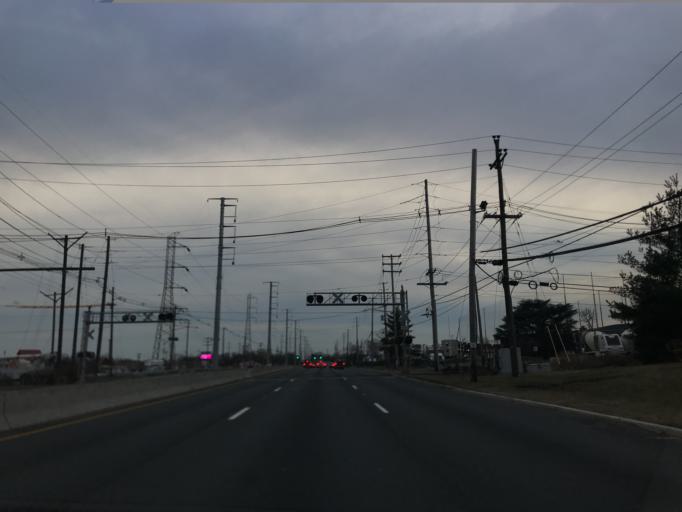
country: US
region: New Jersey
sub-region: Middlesex County
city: Metuchen
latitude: 40.5218
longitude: -74.3635
